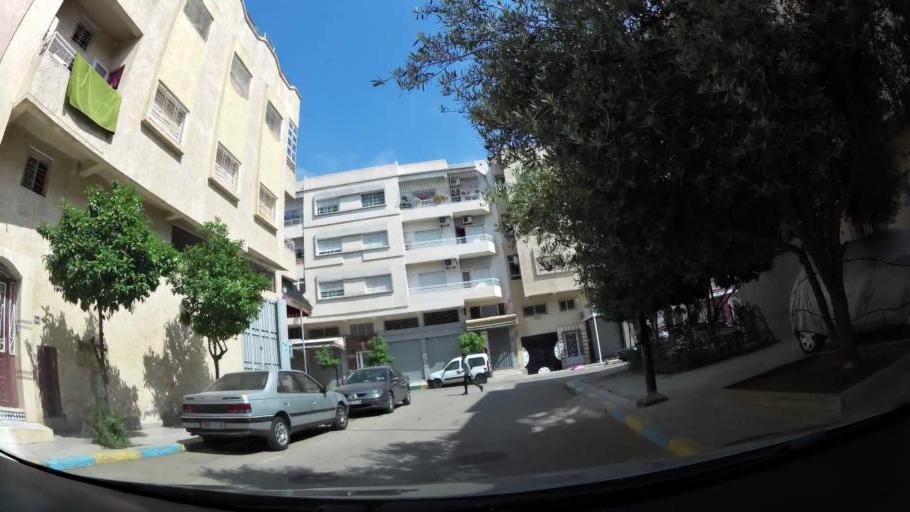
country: MA
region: Fes-Boulemane
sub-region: Fes
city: Fes
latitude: 34.0565
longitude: -5.0294
